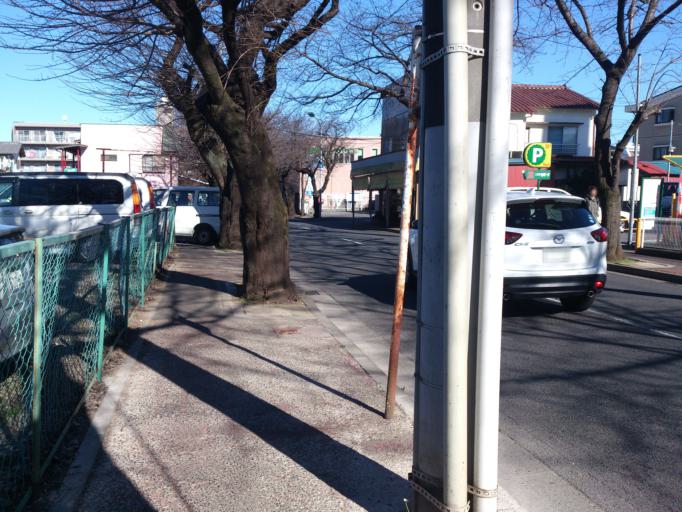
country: JP
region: Chiba
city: Matsudo
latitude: 35.7932
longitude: 139.9394
